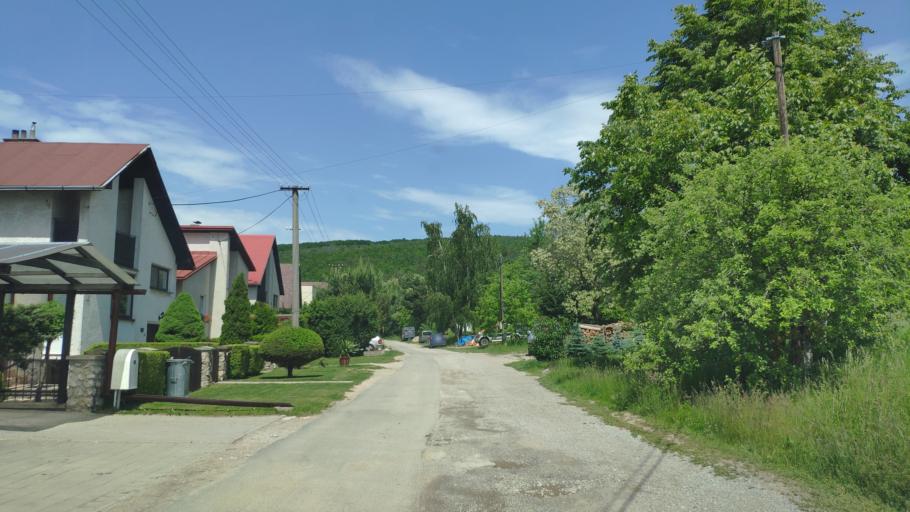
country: SK
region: Kosicky
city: Medzev
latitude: 48.7173
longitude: 20.9709
